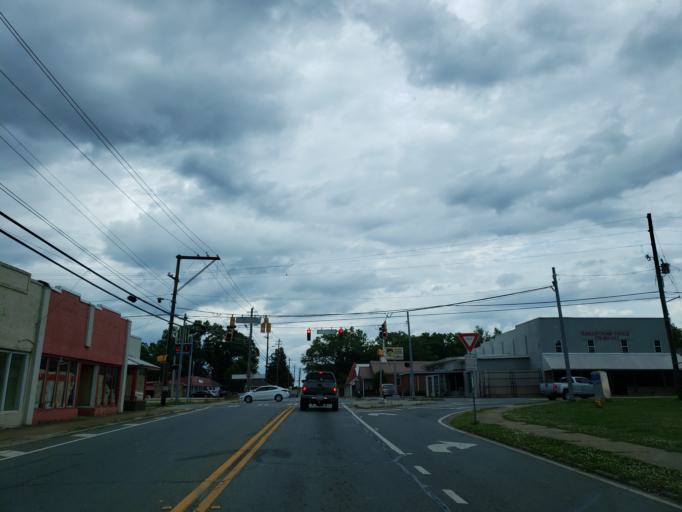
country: US
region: Georgia
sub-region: Polk County
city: Rockmart
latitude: 34.0022
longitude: -85.0414
